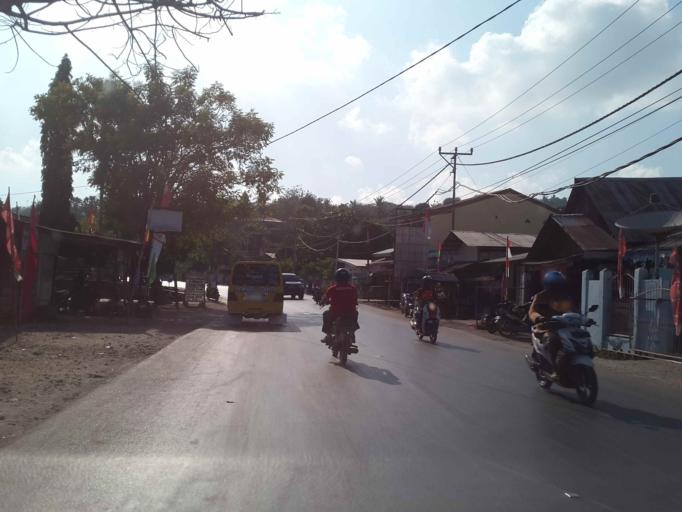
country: ID
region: East Nusa Tenggara
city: Nunbaunsabu
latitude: -10.1715
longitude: 123.5655
